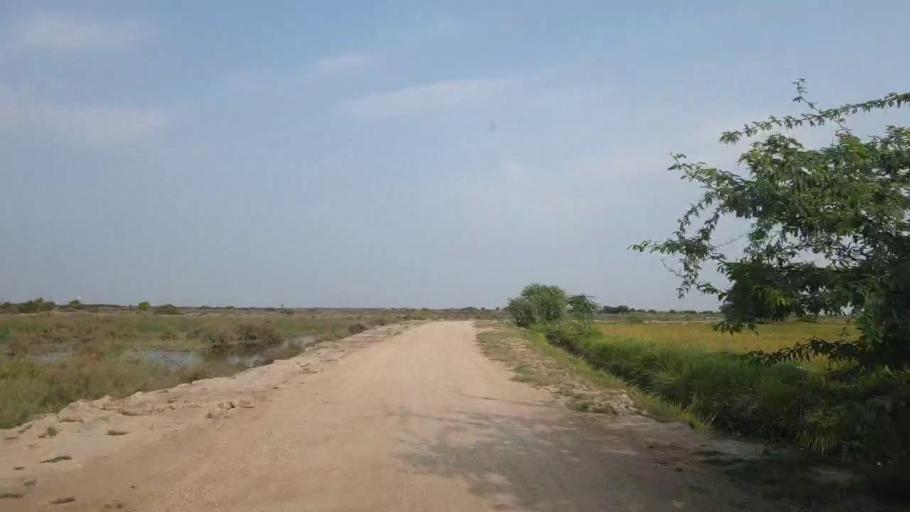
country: PK
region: Sindh
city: Kadhan
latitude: 24.4591
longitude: 68.8015
